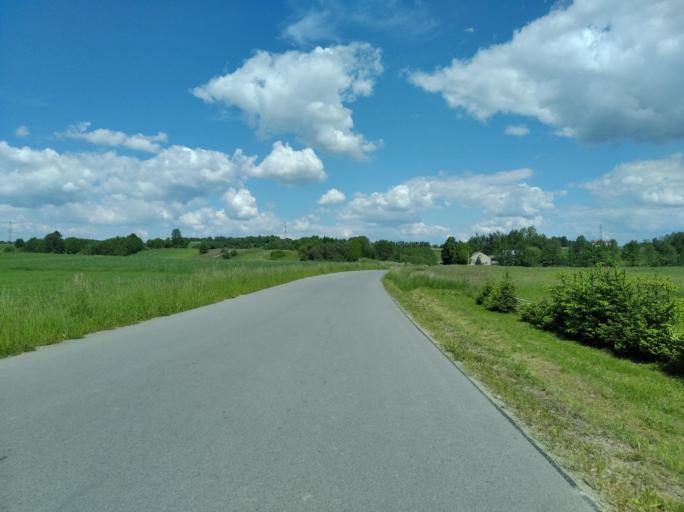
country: PL
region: Subcarpathian Voivodeship
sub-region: Powiat jasielski
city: Tarnowiec
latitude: 49.7674
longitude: 21.6115
